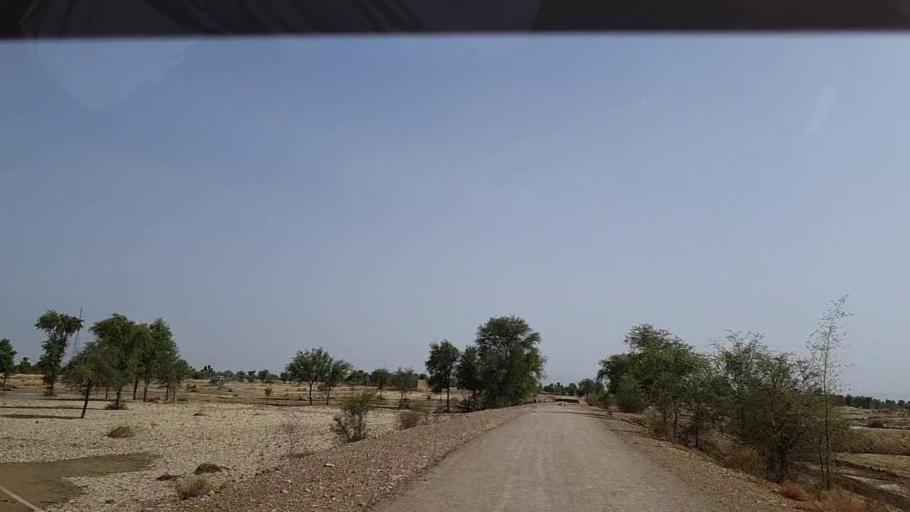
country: PK
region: Sindh
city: Johi
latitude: 26.6430
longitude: 67.5035
